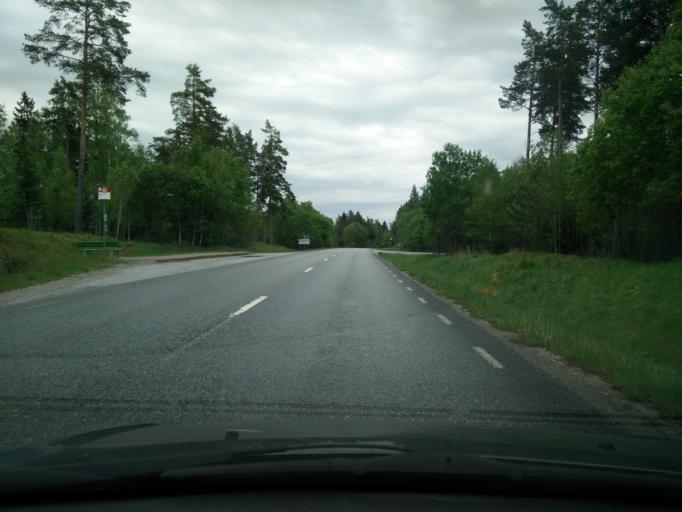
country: SE
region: Stockholm
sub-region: Norrtalje Kommun
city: Bjorko
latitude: 59.8168
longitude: 18.9238
